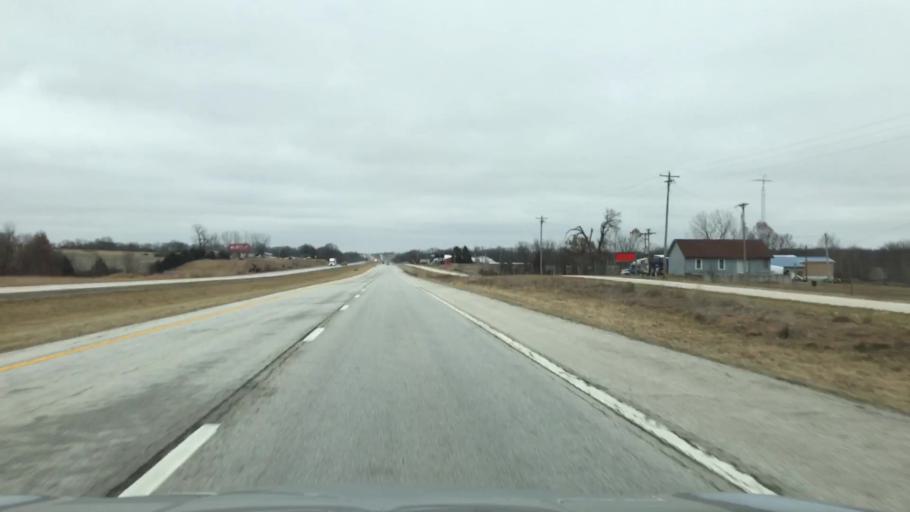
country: US
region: Missouri
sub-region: Linn County
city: Marceline
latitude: 39.7618
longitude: -92.9962
